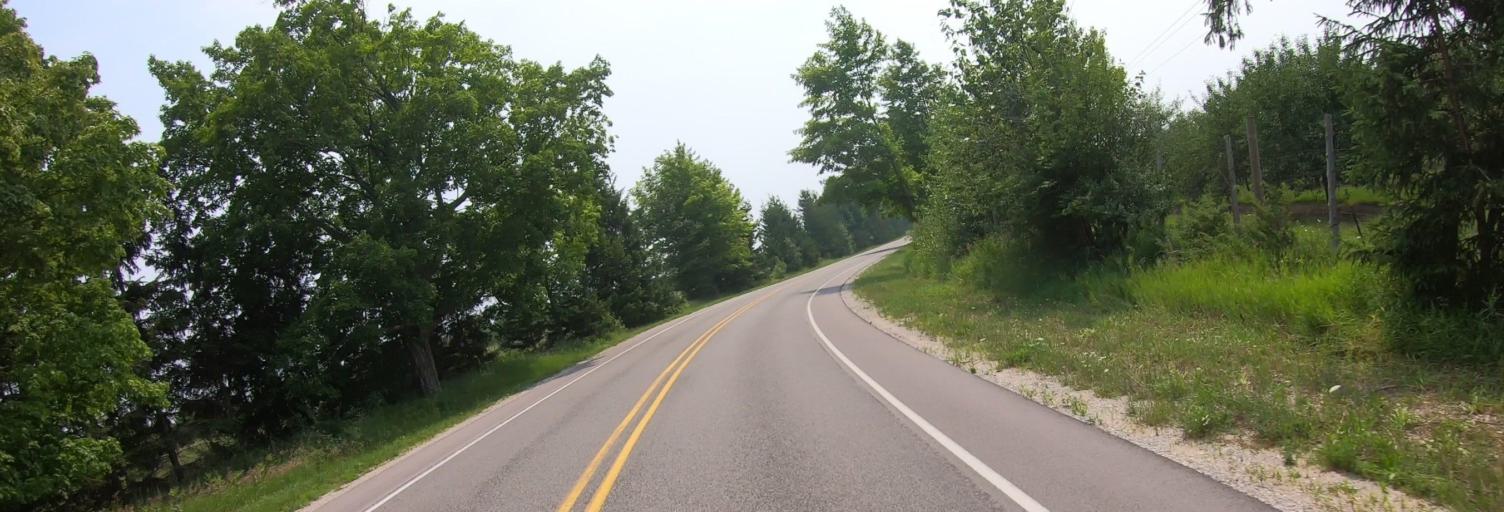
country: US
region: Michigan
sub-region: Leelanau County
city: Leland
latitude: 45.1890
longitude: -85.5406
